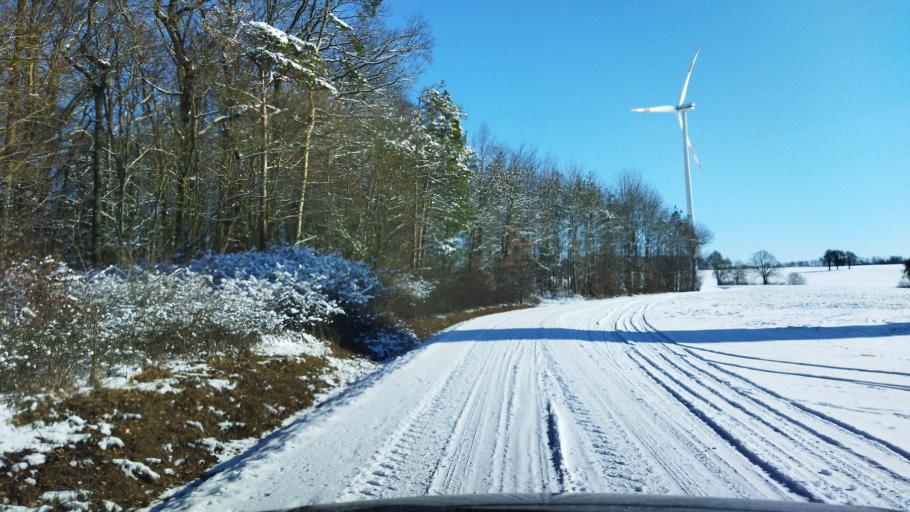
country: DE
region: Baden-Wuerttemberg
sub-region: Regierungsbezirk Stuttgart
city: Ilshofen
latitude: 49.1877
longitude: 9.9469
